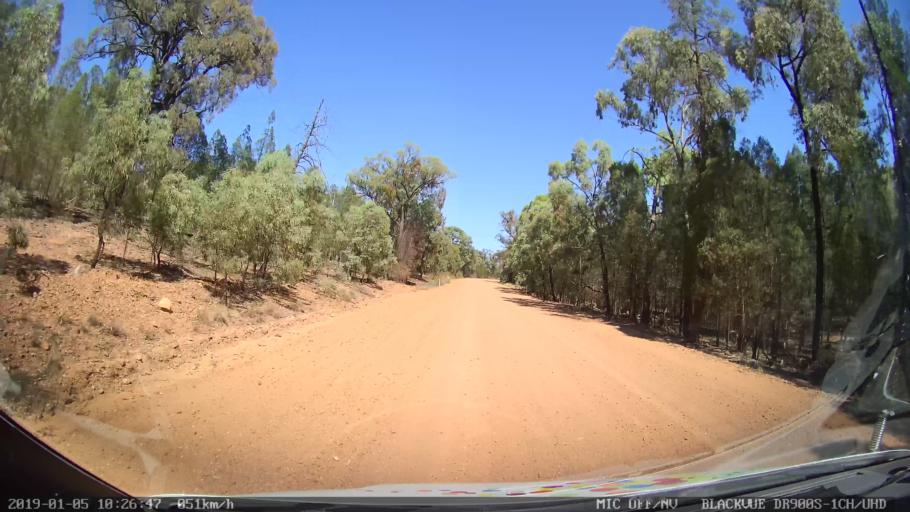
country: AU
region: New South Wales
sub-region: Gilgandra
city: Gilgandra
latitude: -31.5521
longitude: 148.9526
